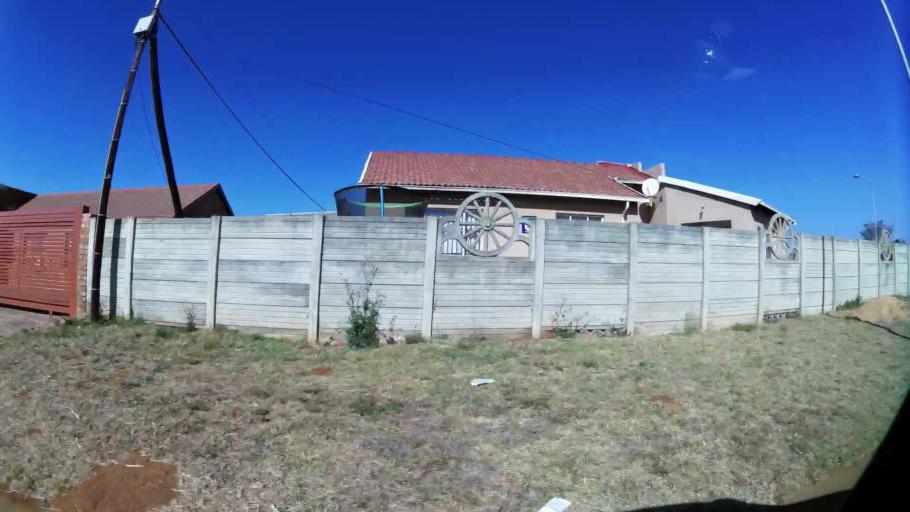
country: ZA
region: North-West
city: Ga-Rankuwa
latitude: -25.6644
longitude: 28.0857
